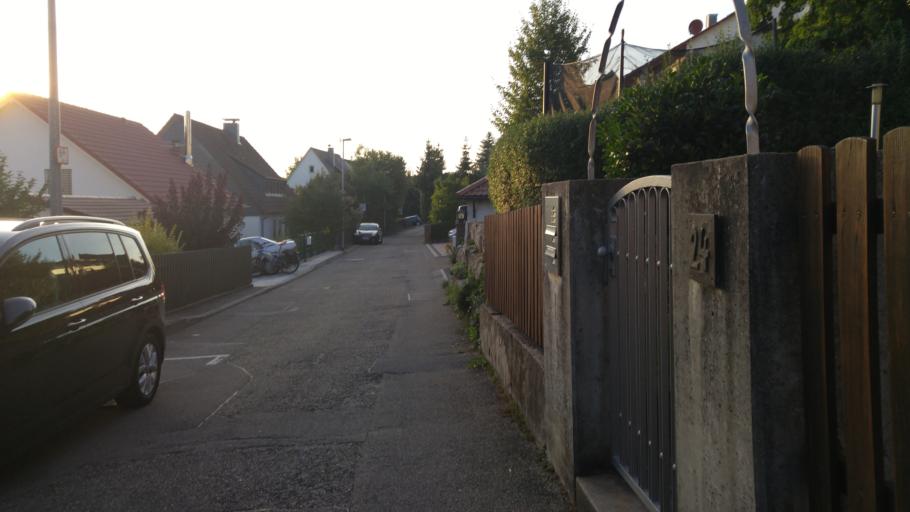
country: DE
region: Baden-Wuerttemberg
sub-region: Regierungsbezirk Stuttgart
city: Leonberg
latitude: 48.8050
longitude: 9.0128
